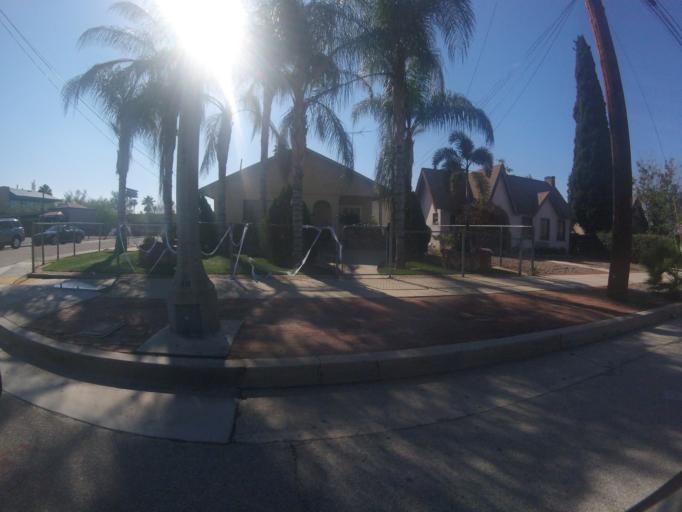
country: US
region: California
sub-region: San Bernardino County
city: Redlands
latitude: 34.0628
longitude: -117.1866
